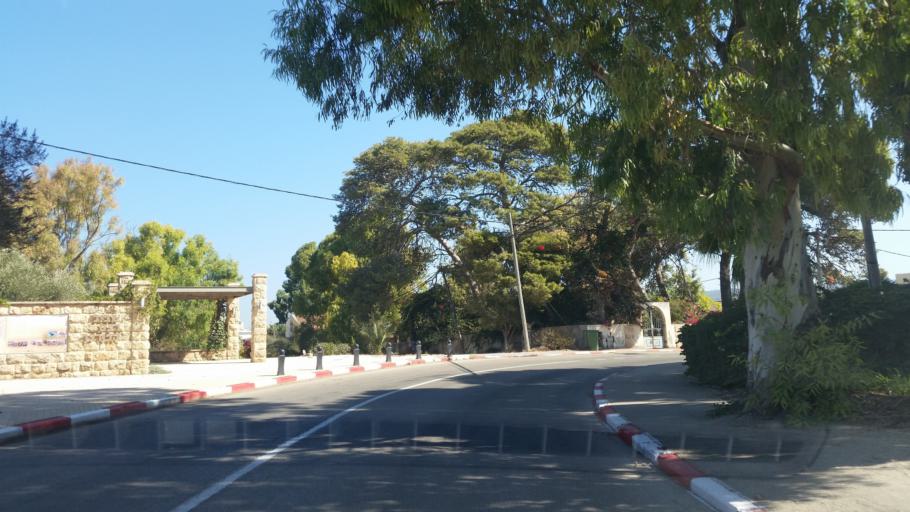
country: IL
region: Haifa
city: `Atlit
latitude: 32.6923
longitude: 34.9424
